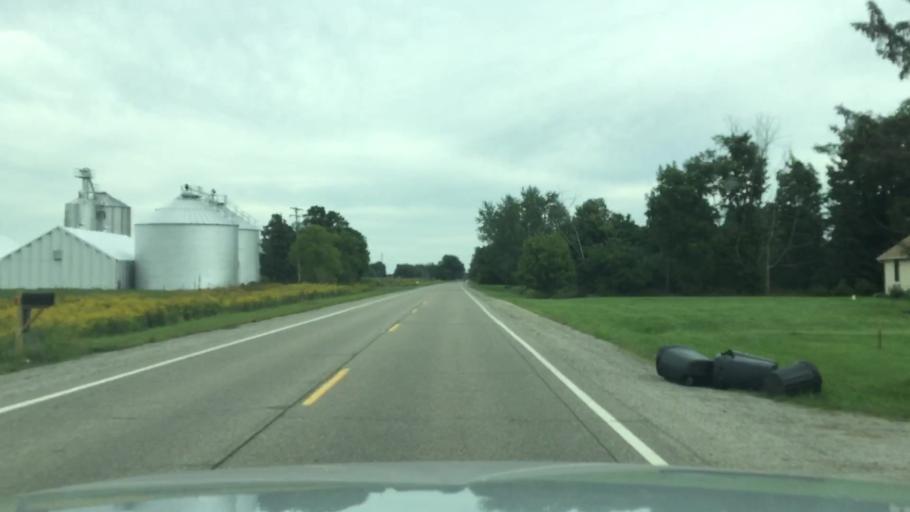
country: US
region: Michigan
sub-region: Genesee County
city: Swartz Creek
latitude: 42.9570
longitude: -83.9036
